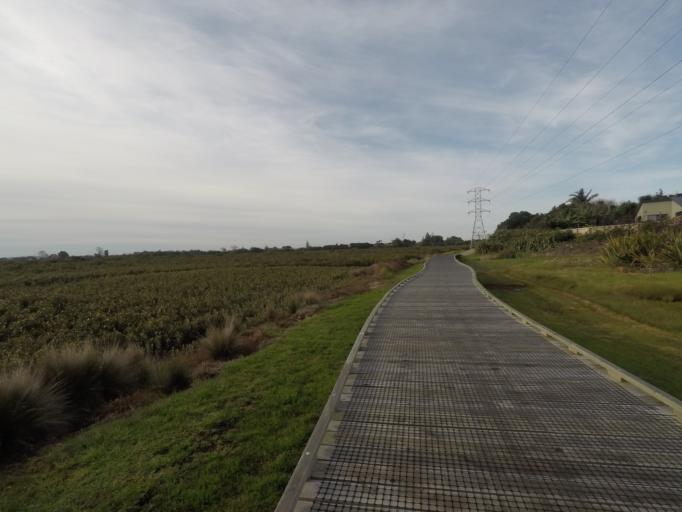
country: NZ
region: Auckland
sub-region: Auckland
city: Mangere
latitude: -36.9429
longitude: 174.7979
